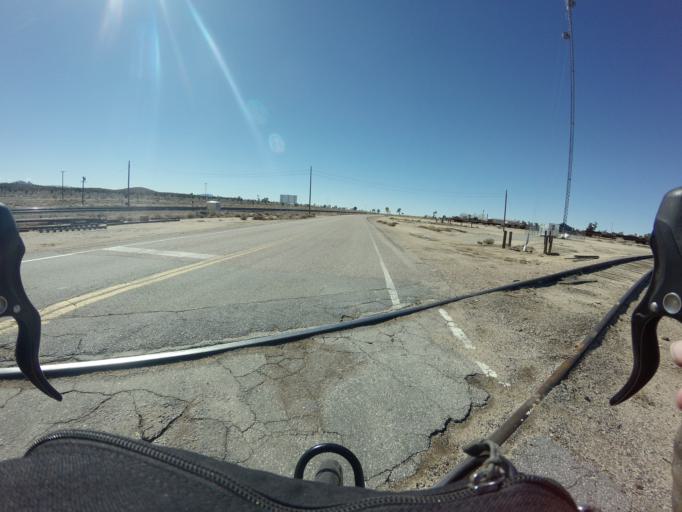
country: US
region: Nevada
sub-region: Clark County
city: Sandy Valley
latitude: 35.2363
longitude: -115.5008
